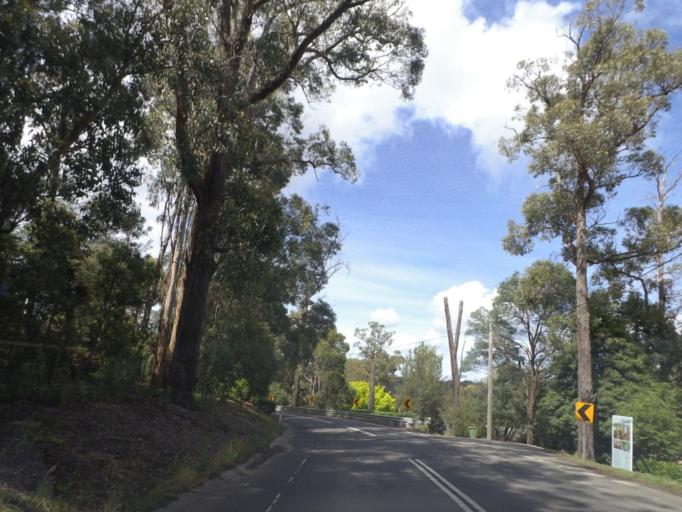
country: AU
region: Victoria
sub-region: Cardinia
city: Cockatoo
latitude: -37.9237
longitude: 145.4732
